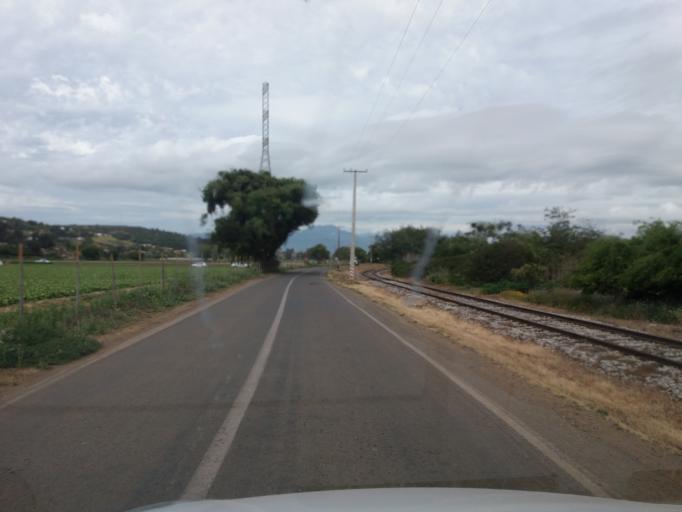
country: CL
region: Valparaiso
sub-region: Provincia de Marga Marga
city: Villa Alemana
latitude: -32.9168
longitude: -71.4009
